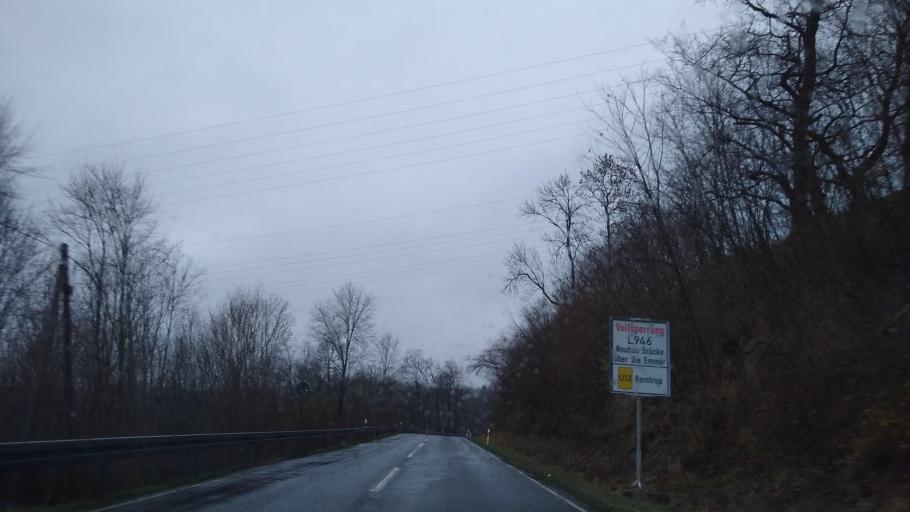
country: DE
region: North Rhine-Westphalia
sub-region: Regierungsbezirk Detmold
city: Lugde
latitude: 51.9331
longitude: 9.2333
